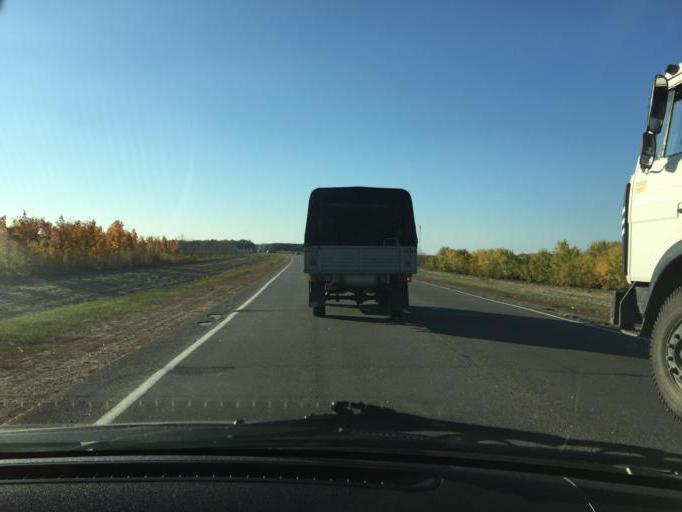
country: BY
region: Brest
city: Luninyets
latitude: 52.2744
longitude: 26.9790
